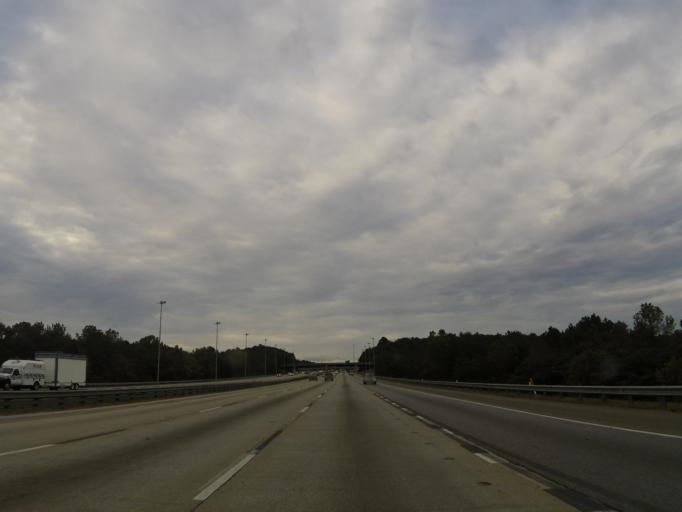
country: US
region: Alabama
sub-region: Jefferson County
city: Hoover
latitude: 33.3819
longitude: -86.7819
